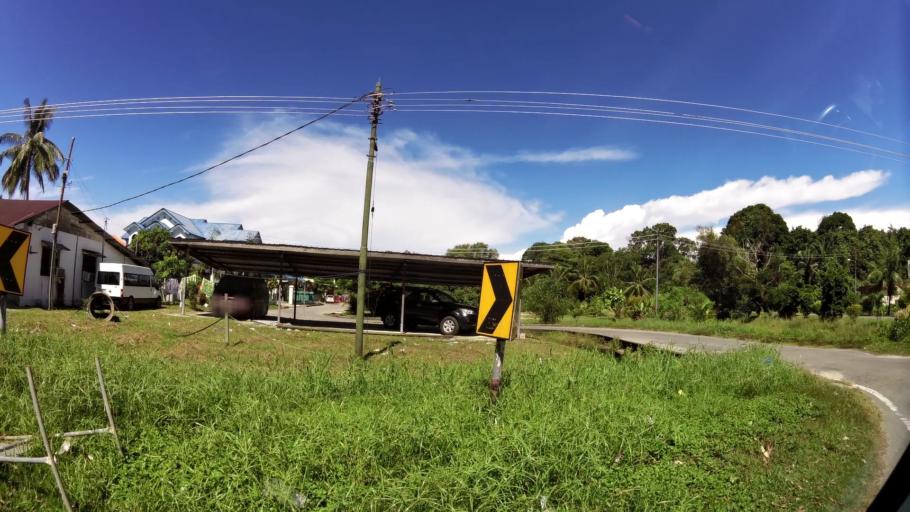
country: BN
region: Brunei and Muara
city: Bandar Seri Begawan
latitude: 5.0089
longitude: 115.0594
